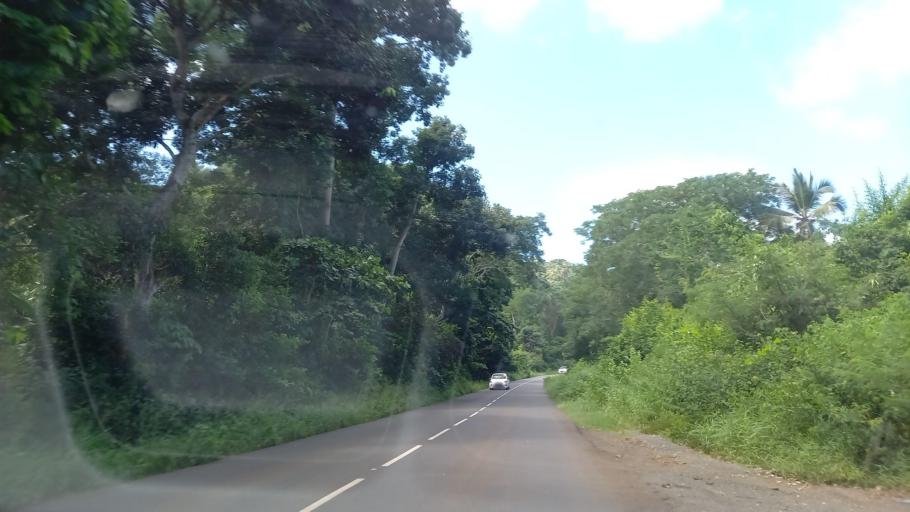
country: YT
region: M'Tsangamouji
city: M'Tsangamouji
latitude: -12.7485
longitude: 45.0622
